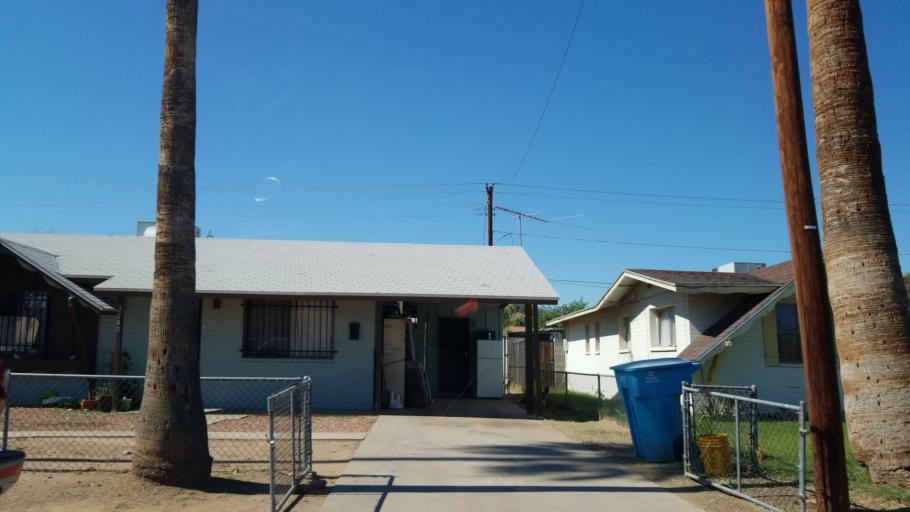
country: US
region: Arizona
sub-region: Maricopa County
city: Glendale
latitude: 33.4748
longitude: -112.1643
